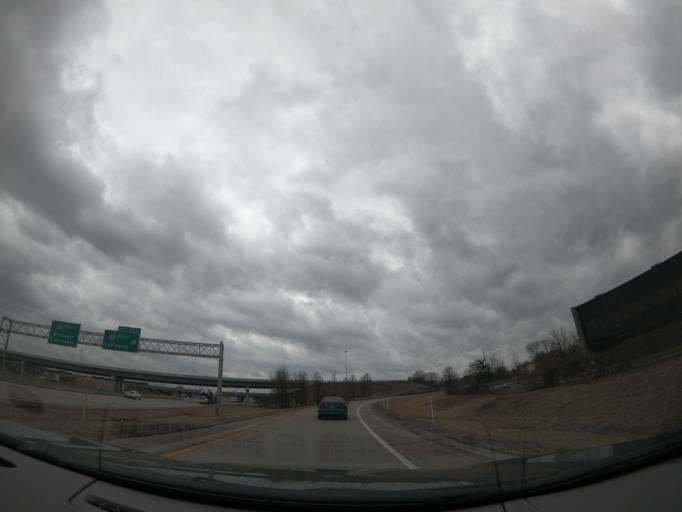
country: US
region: Kentucky
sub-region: Jefferson County
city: Saint Regis Park
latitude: 38.2409
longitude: -85.6230
